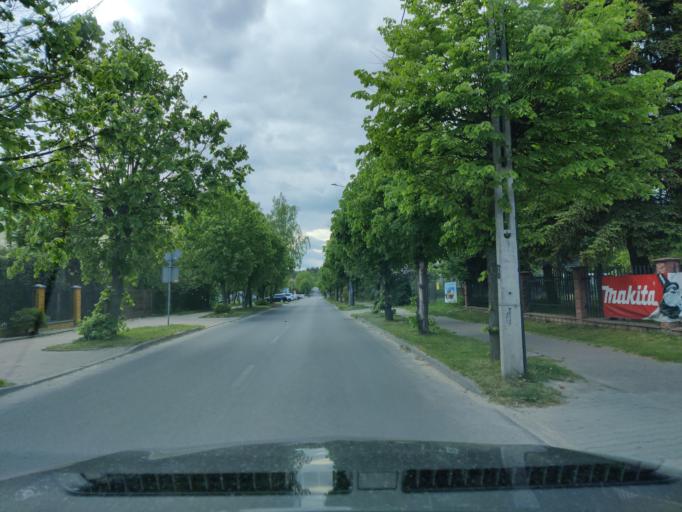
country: PL
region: Swietokrzyskie
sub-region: Powiat skarzyski
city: Skarzysko-Kamienna
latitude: 51.1193
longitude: 20.8579
